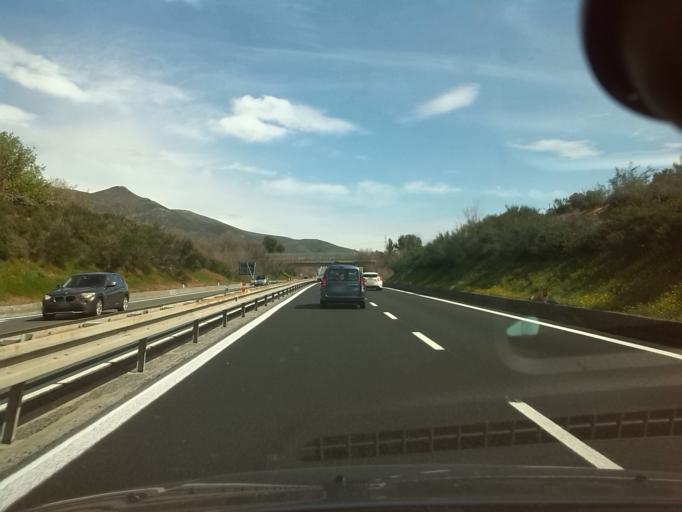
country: IT
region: Liguria
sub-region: Provincia di Savona
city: Campochiesa
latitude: 44.0776
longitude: 8.1909
